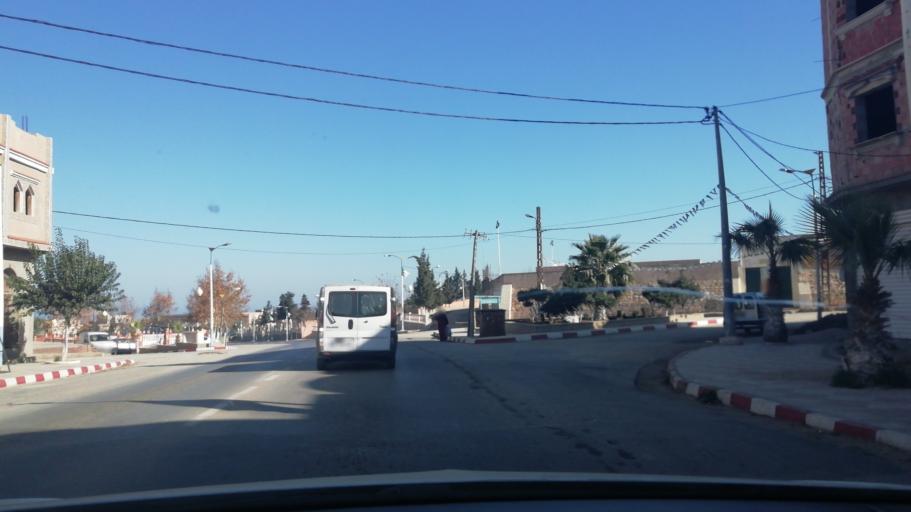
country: DZ
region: Tlemcen
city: Nedroma
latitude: 35.0496
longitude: -1.8788
